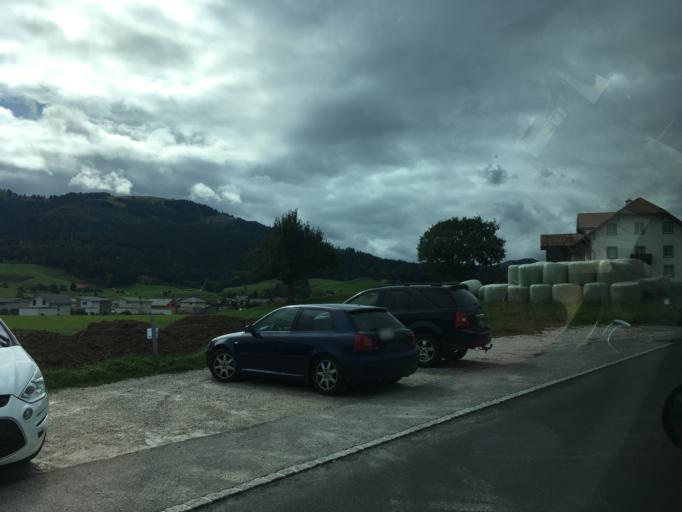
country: CH
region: Fribourg
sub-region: Sense District
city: Plaffeien
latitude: 46.7427
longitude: 7.2816
